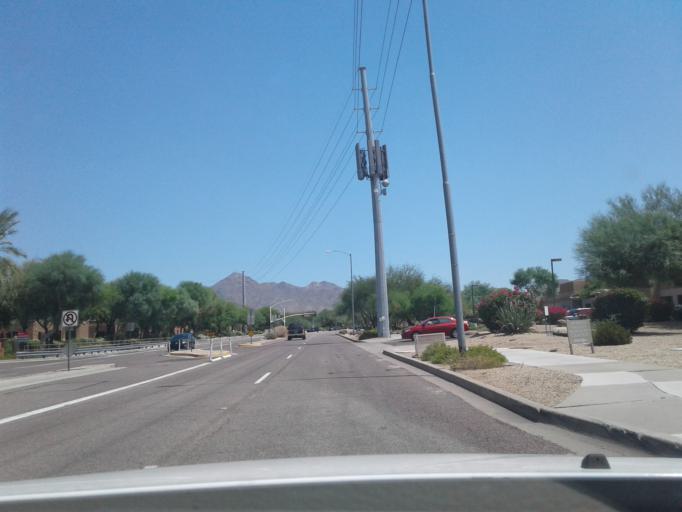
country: US
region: Arizona
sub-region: Maricopa County
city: Paradise Valley
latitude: 33.6183
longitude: -111.8894
